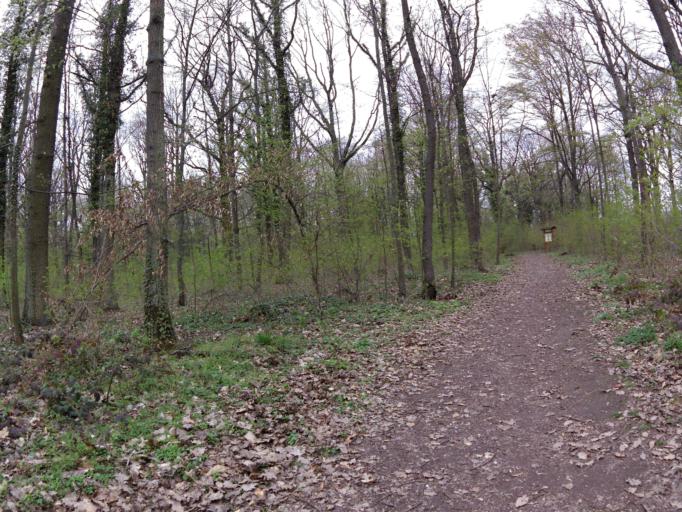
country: DE
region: Bavaria
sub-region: Regierungsbezirk Unterfranken
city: Rottendorf
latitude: 49.7993
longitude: 10.0178
